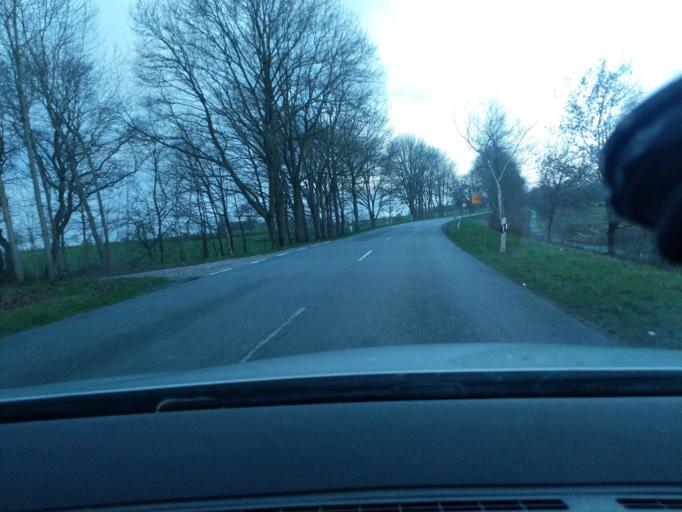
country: DE
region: Lower Saxony
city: Lintig
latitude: 53.6113
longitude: 8.8507
